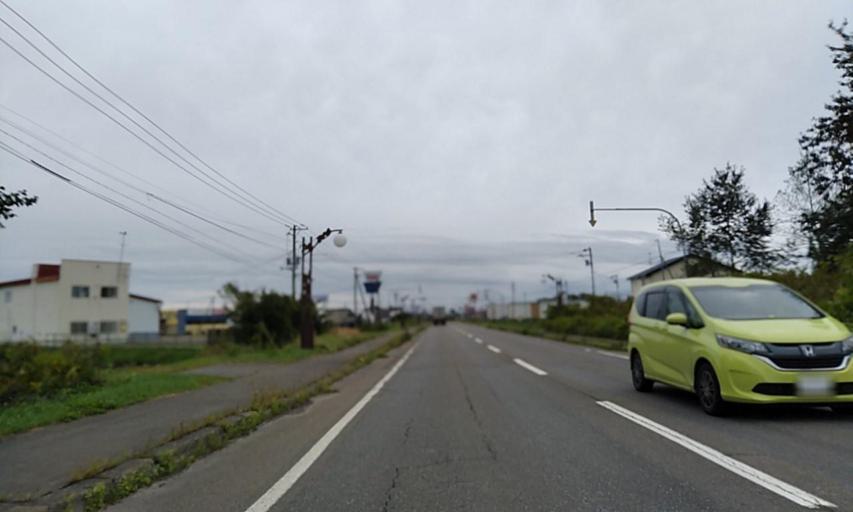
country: JP
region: Hokkaido
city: Obihiro
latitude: 42.4841
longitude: 143.2723
